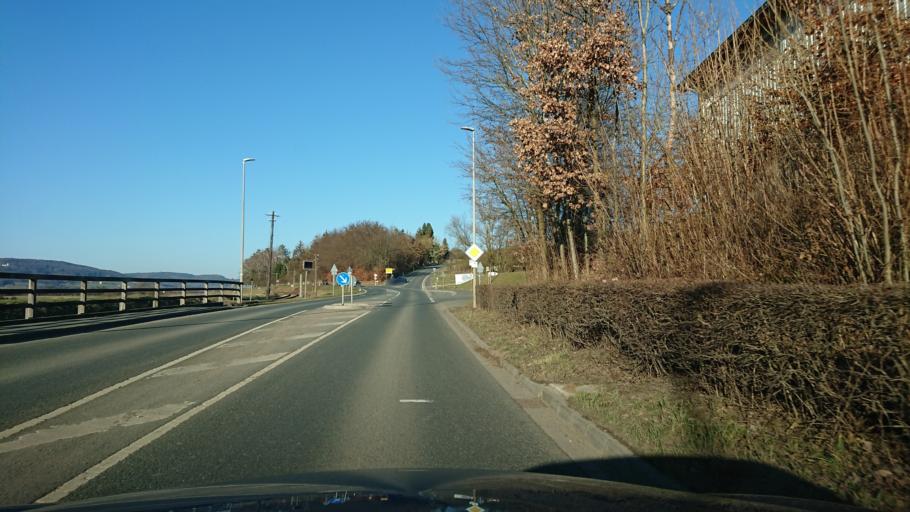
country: DE
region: Bavaria
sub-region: Upper Franconia
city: Wiesenthau
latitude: 49.7143
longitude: 11.1281
